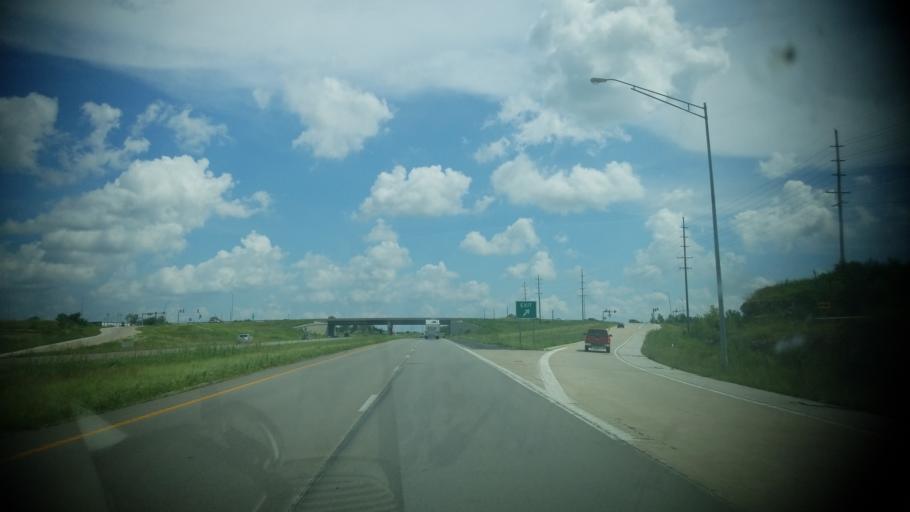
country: US
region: Missouri
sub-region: Lincoln County
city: Moscow Mills
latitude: 38.9115
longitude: -90.9241
